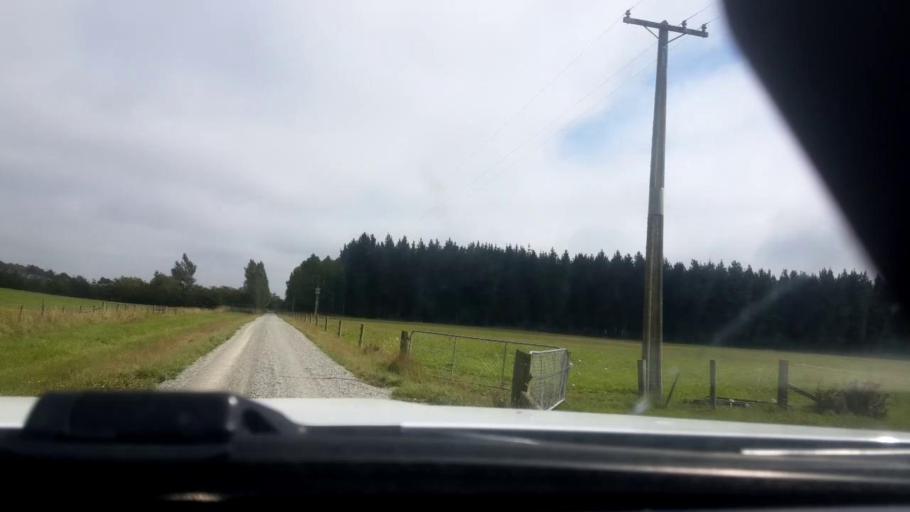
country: NZ
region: Canterbury
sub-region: Timaru District
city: Timaru
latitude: -44.3298
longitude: 171.1983
